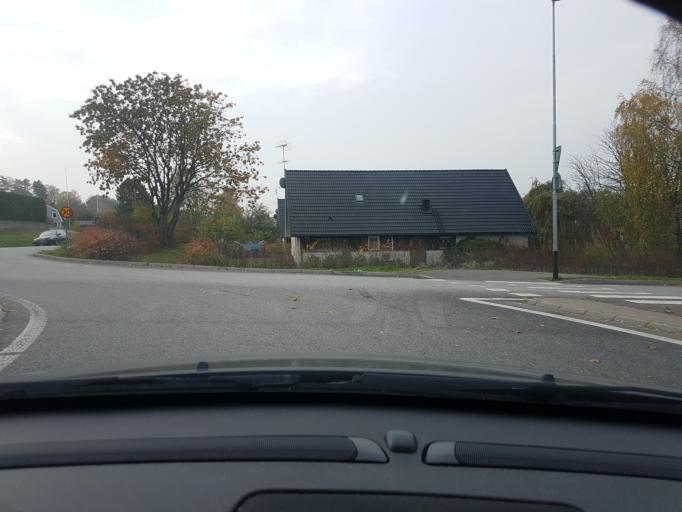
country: SE
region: Vaestra Goetaland
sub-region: Ale Kommun
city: Alvangen
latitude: 57.9486
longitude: 12.1053
